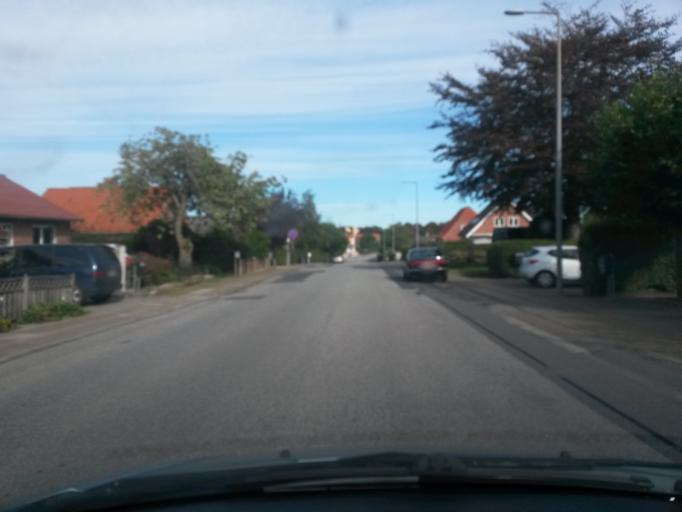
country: DK
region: Central Jutland
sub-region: Silkeborg Kommune
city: Kjellerup
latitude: 56.2873
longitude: 9.4176
